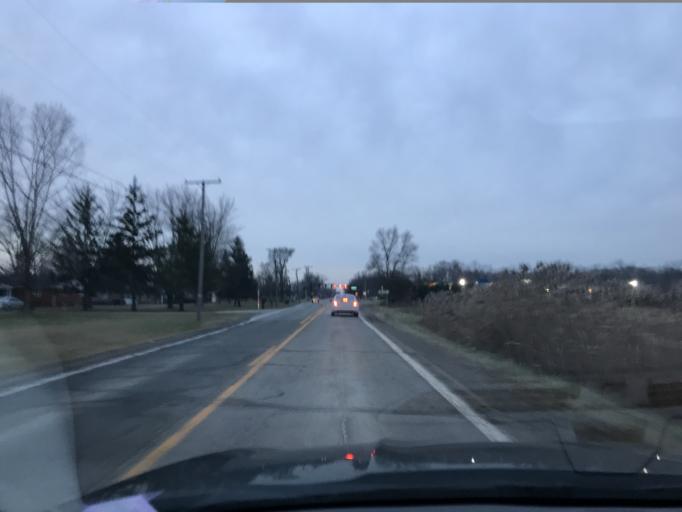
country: US
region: Michigan
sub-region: Macomb County
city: Romeo
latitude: 42.8077
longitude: -82.9626
